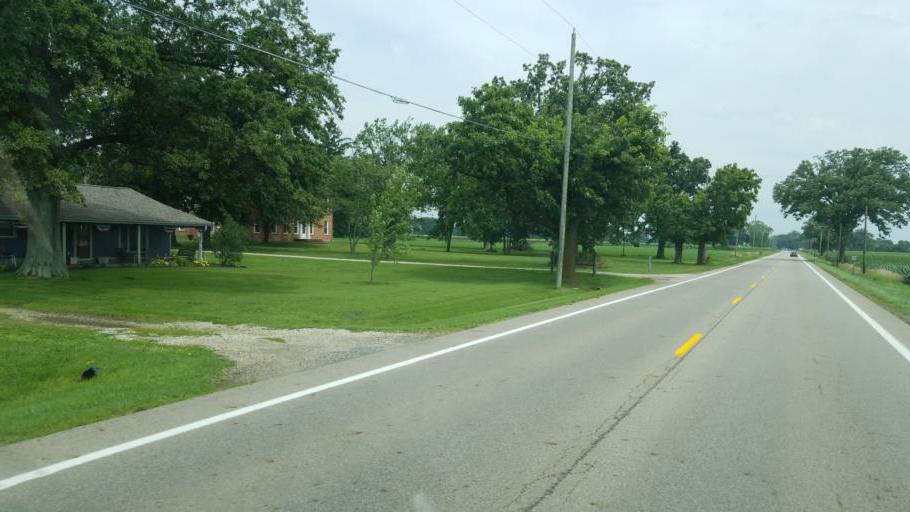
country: US
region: Ohio
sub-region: Madison County
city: Plain City
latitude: 40.0917
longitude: -83.2817
